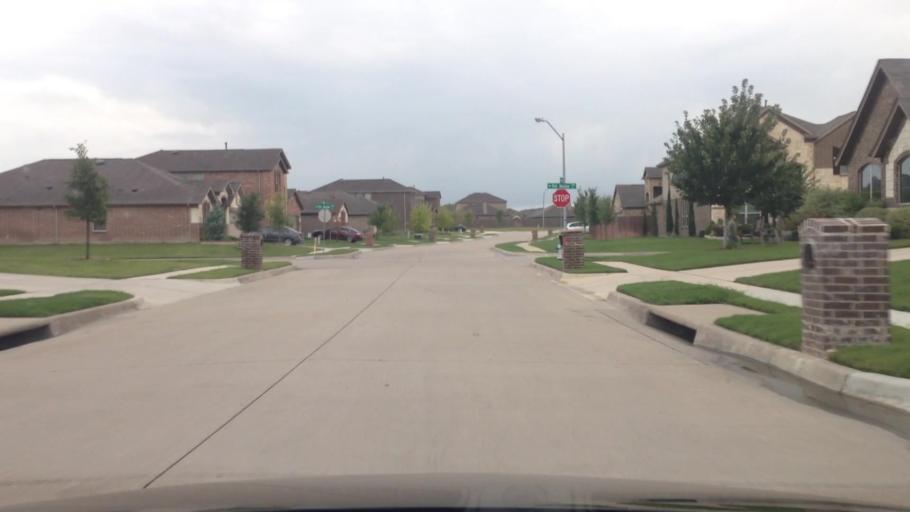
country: US
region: Texas
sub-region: Tarrant County
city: Crowley
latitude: 32.5685
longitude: -97.3363
